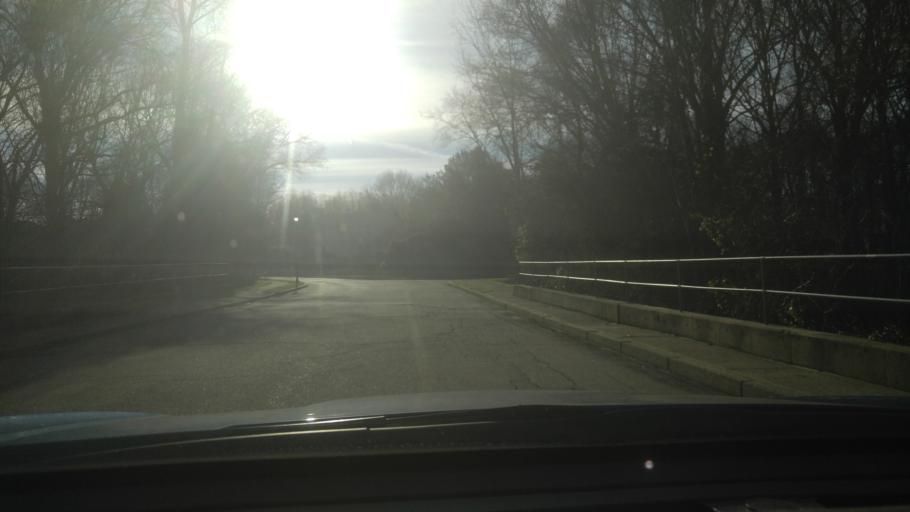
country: US
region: Rhode Island
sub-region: Kent County
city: East Greenwich
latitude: 41.6802
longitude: -71.4696
